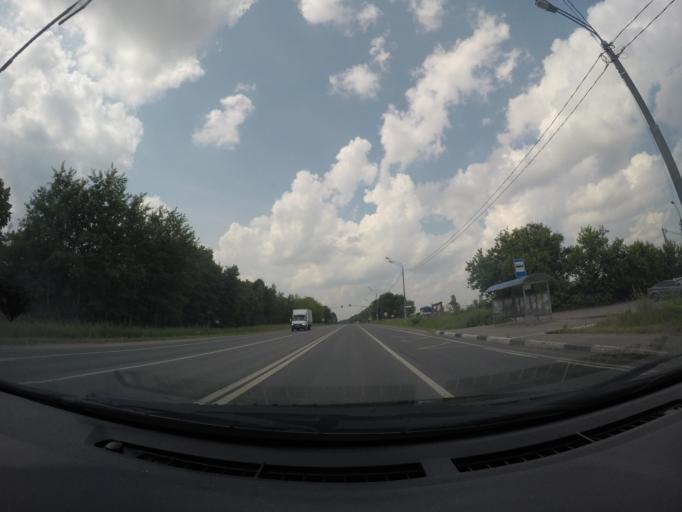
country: RU
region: Moskovskaya
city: Bronnitsy
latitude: 55.4745
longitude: 38.1887
